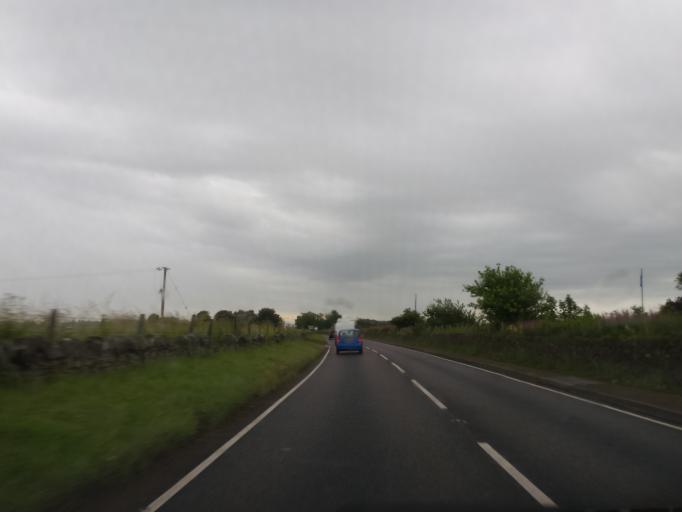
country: GB
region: Scotland
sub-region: Fife
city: Leuchars
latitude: 56.3871
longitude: -2.8966
